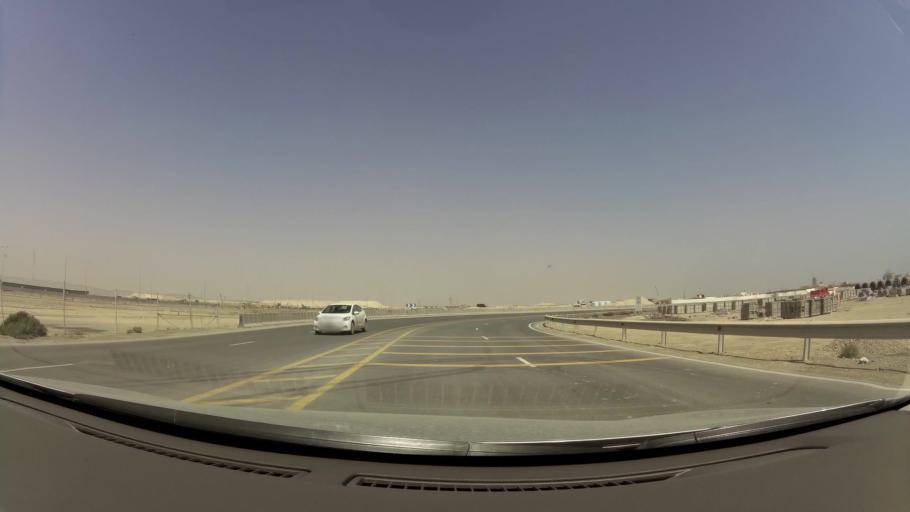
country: QA
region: Baladiyat Umm Salal
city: Umm Salal Muhammad
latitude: 25.4007
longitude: 51.4948
